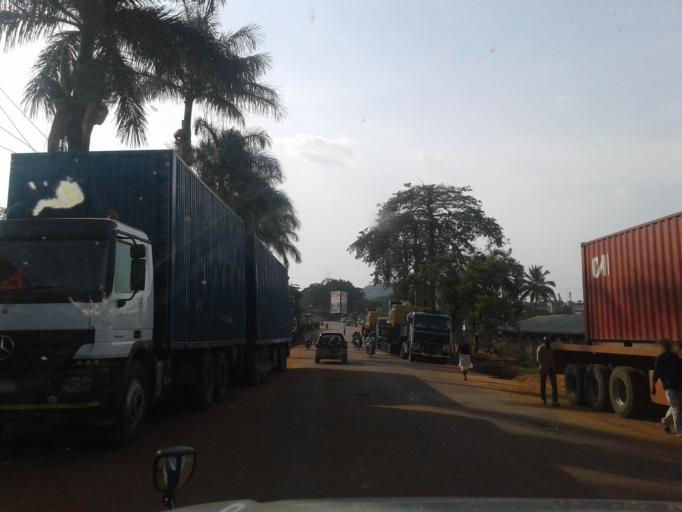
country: UG
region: Central Region
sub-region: Wakiso District
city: Kireka
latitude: 0.3322
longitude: 32.6198
